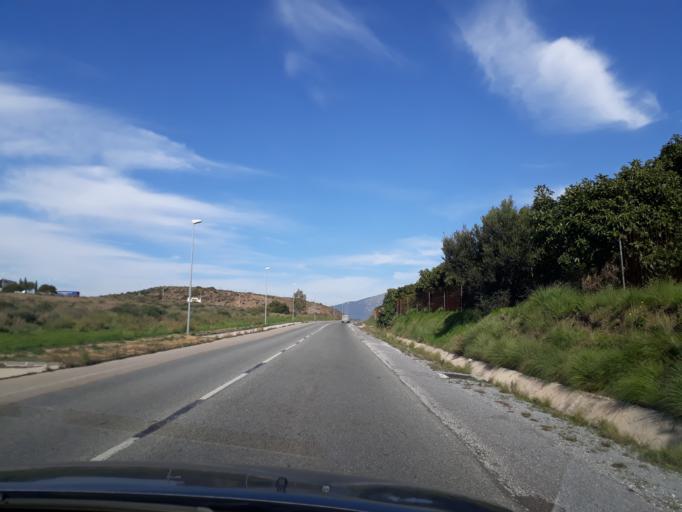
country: ES
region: Andalusia
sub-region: Provincia de Malaga
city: Fuengirola
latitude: 36.5287
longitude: -4.6860
